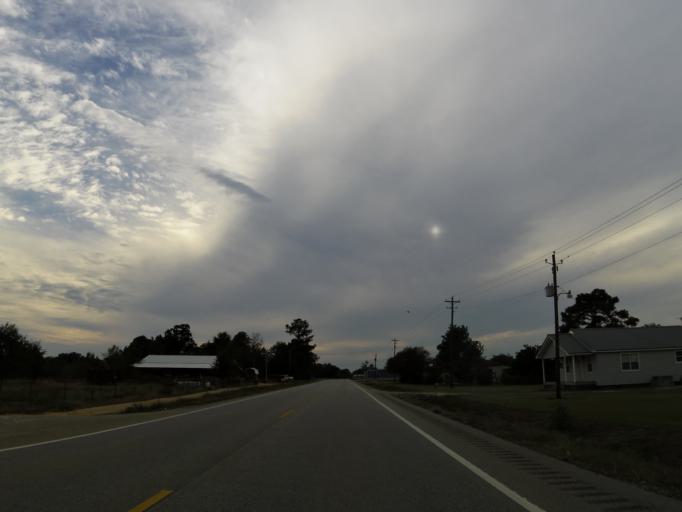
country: US
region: Alabama
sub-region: Monroe County
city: Frisco City
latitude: 31.3102
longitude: -87.4876
